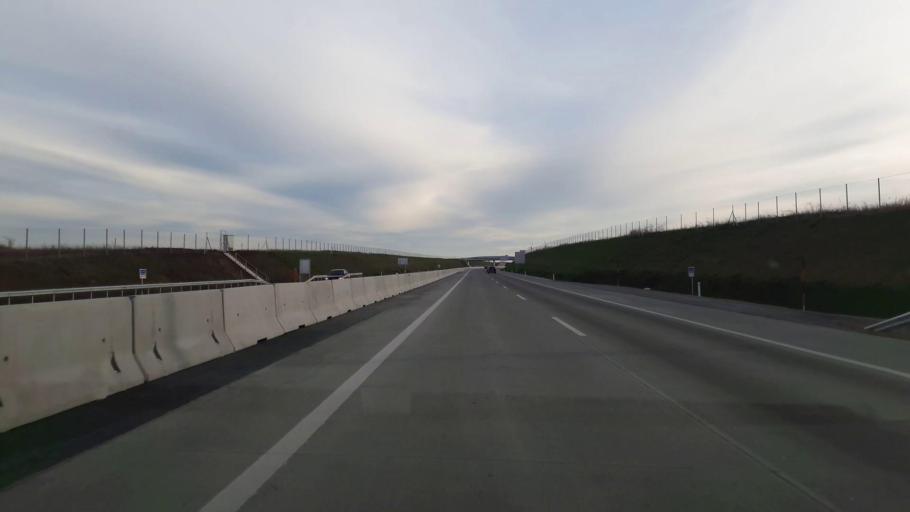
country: AT
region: Lower Austria
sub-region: Politischer Bezirk Mistelbach
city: Wilfersdorf
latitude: 48.5711
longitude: 16.6286
